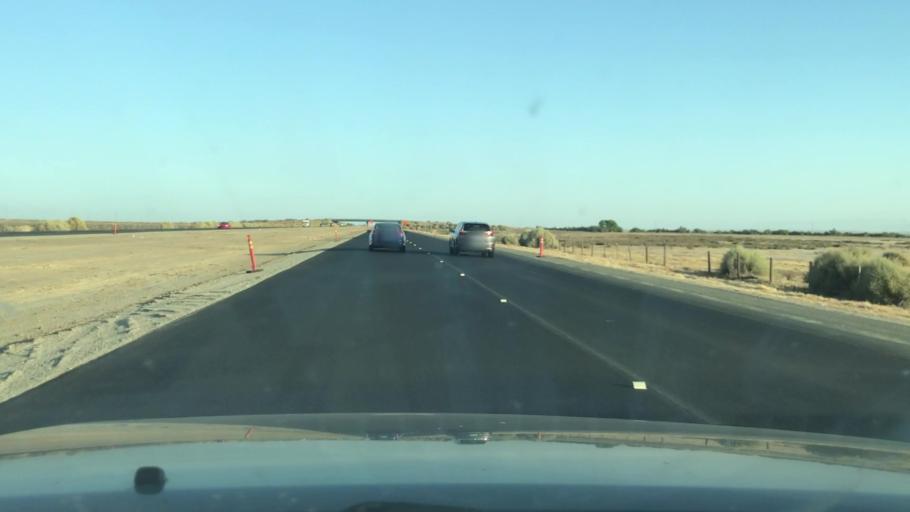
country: US
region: California
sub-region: Kern County
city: Lost Hills
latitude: 35.7964
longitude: -119.7877
